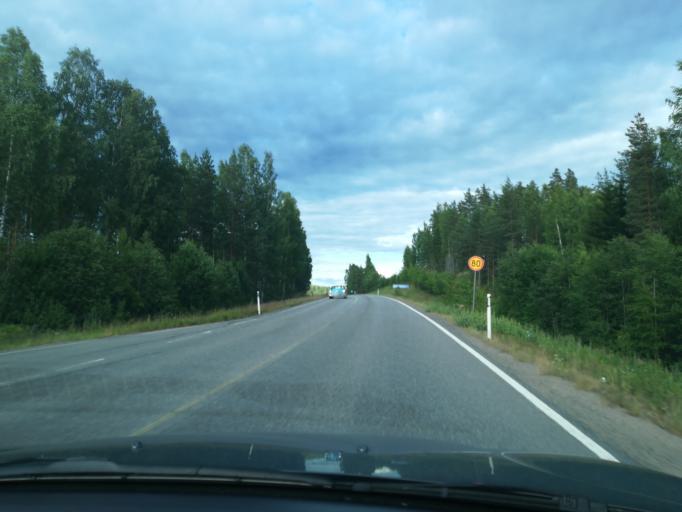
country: FI
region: South Karelia
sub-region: Lappeenranta
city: Savitaipale
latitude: 61.5380
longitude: 27.6955
